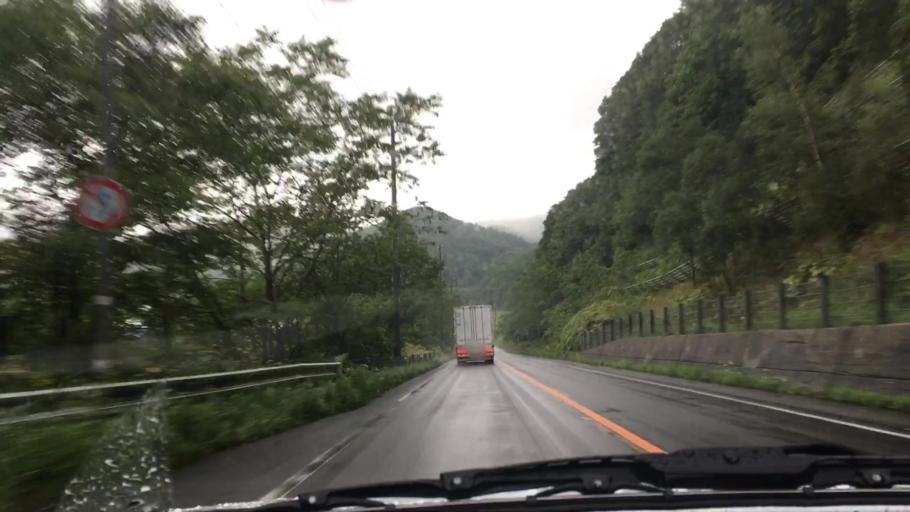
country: JP
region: Hokkaido
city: Niseko Town
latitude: 42.5977
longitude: 140.5884
